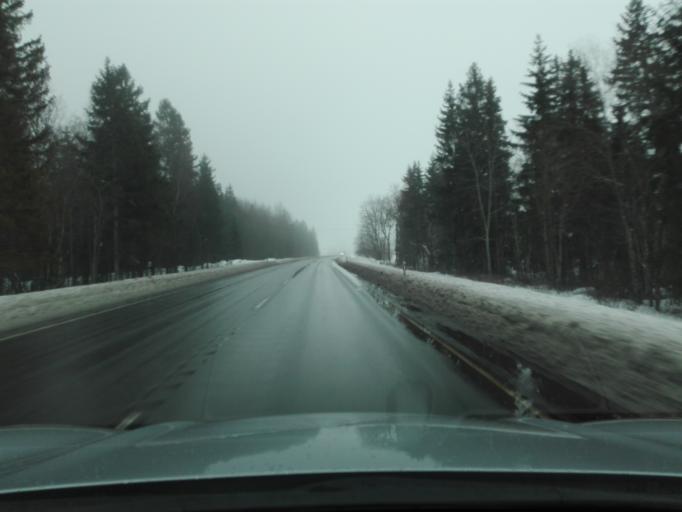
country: EE
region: Raplamaa
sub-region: Kohila vald
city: Kohila
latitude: 59.2261
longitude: 24.7773
